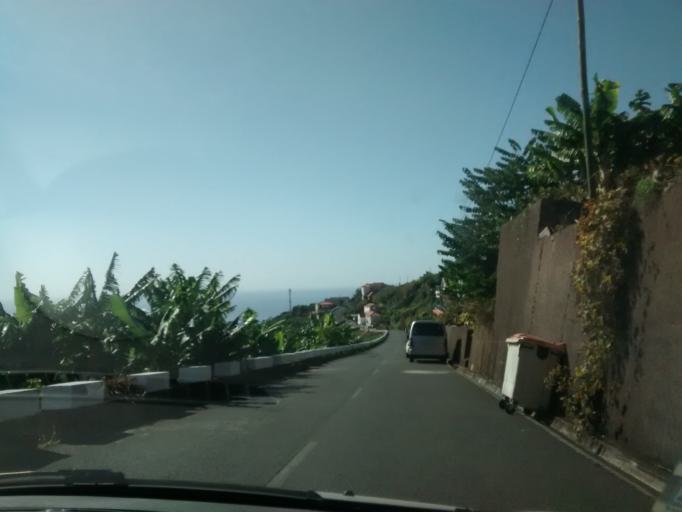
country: PT
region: Madeira
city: Calheta
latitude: 32.7235
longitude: -17.1689
